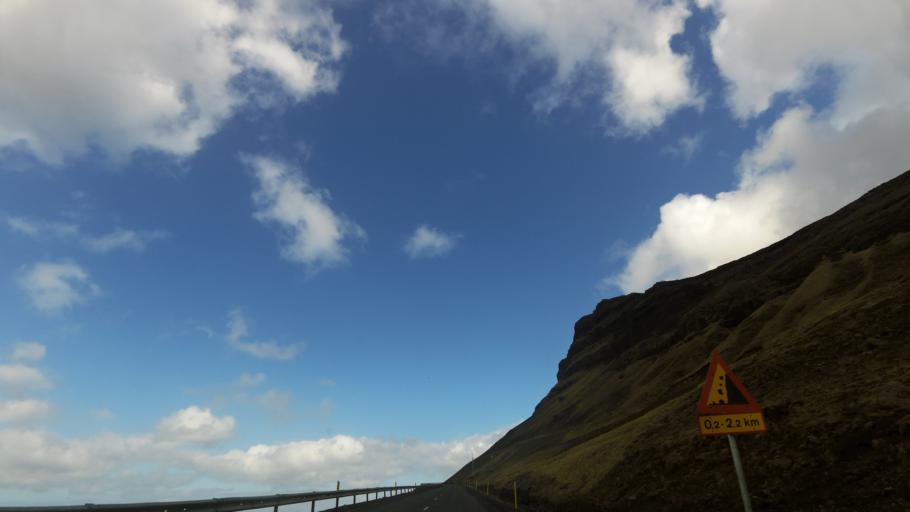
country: IS
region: West
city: Olafsvik
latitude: 64.9395
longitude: -23.5006
